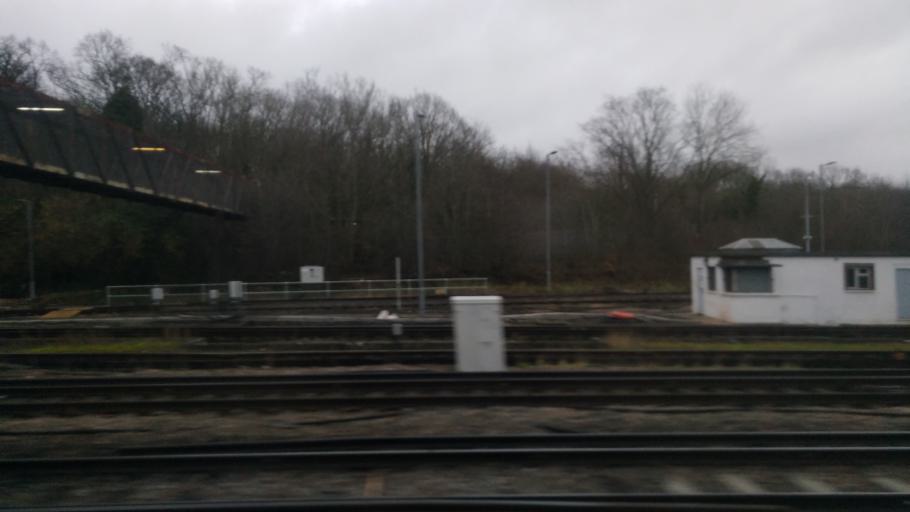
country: GB
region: England
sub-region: Greater London
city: Bromley
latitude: 51.4355
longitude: 0.0156
